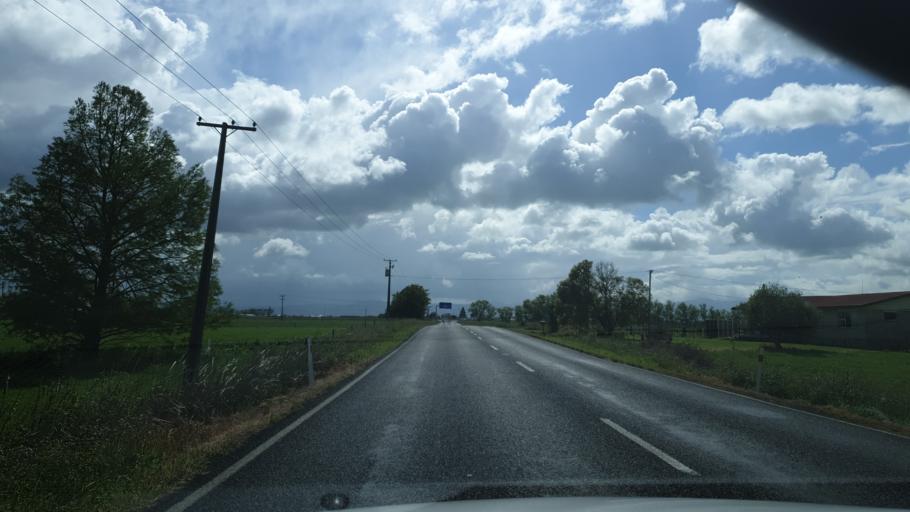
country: NZ
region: Waikato
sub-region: Hauraki District
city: Paeroa
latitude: -37.5118
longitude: 175.5189
